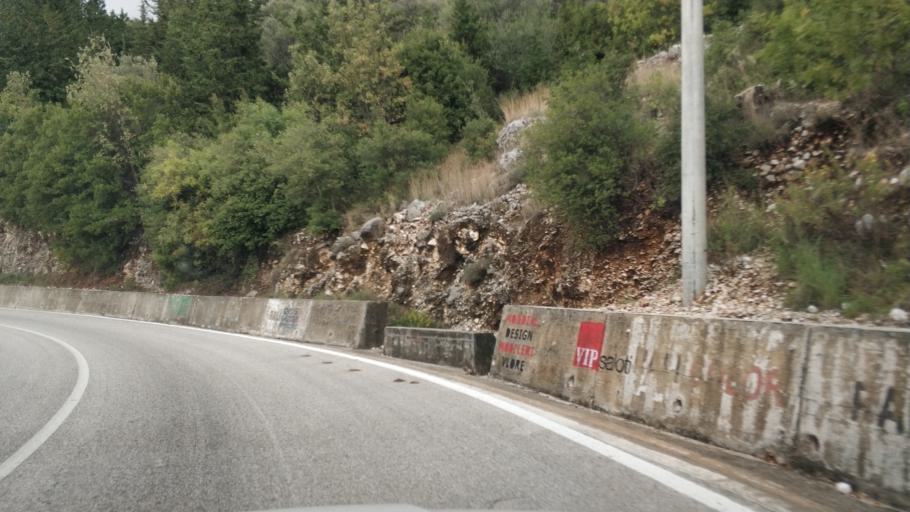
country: AL
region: Vlore
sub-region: Rrethi i Vlores
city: Vranisht
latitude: 40.1700
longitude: 19.6167
